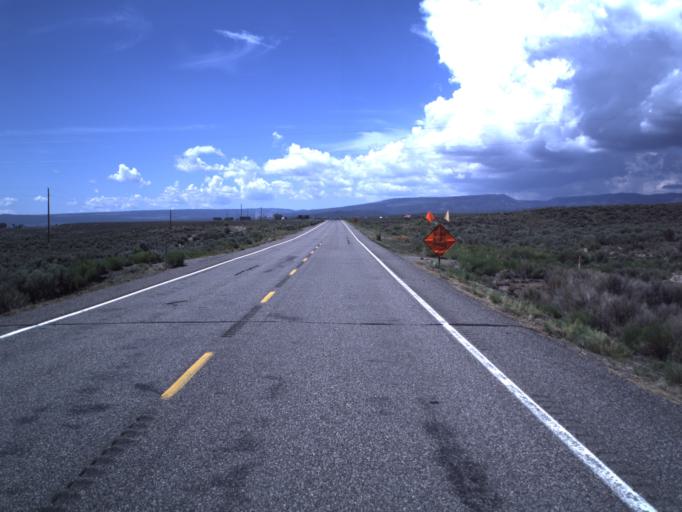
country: US
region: Utah
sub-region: Garfield County
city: Panguitch
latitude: 37.9744
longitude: -112.4061
